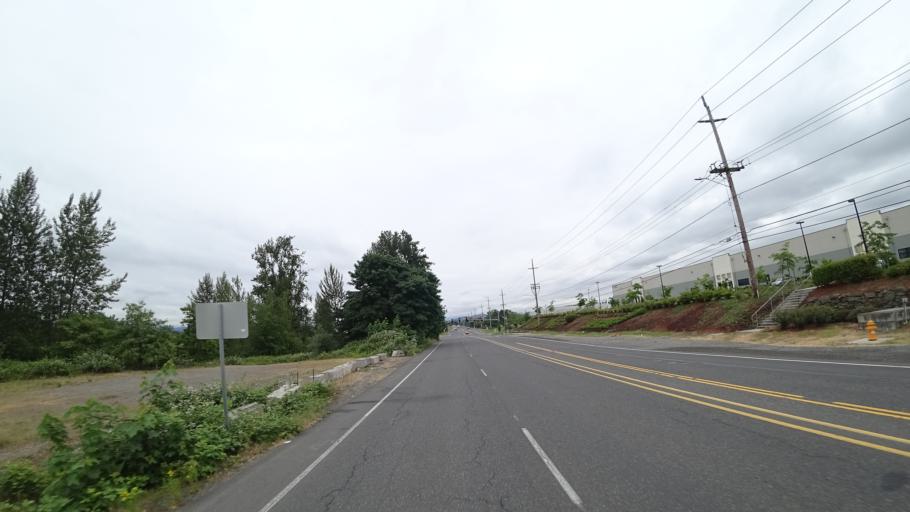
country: US
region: Oregon
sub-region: Multnomah County
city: Fairview
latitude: 45.5458
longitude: -122.4739
